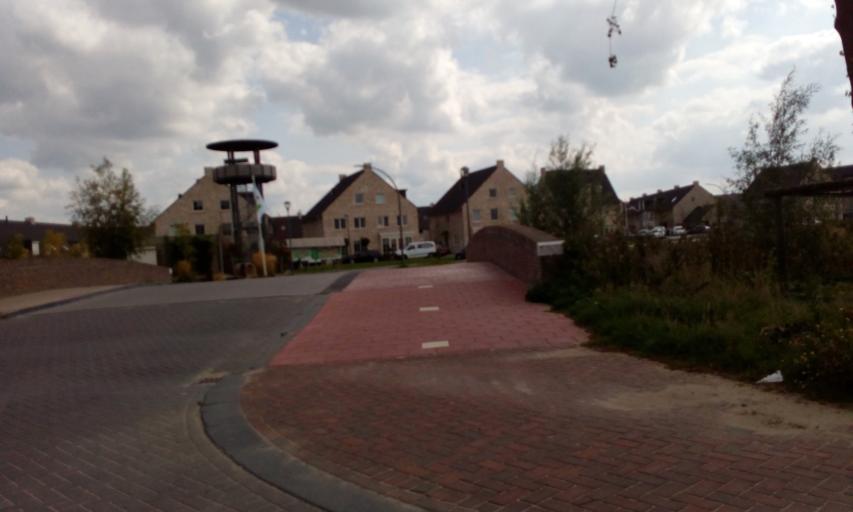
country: NL
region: South Holland
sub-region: Gemeente Waddinxveen
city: Waddinxveen
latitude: 52.0334
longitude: 4.6424
